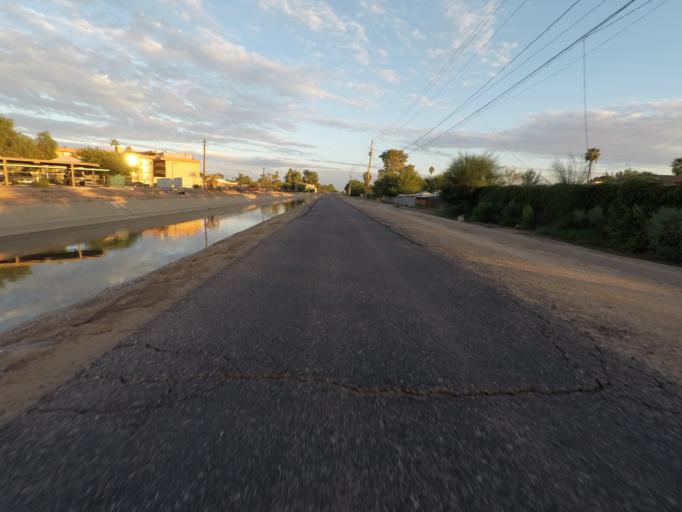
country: US
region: Arizona
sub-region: Maricopa County
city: Phoenix
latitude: 33.4796
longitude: -112.0333
